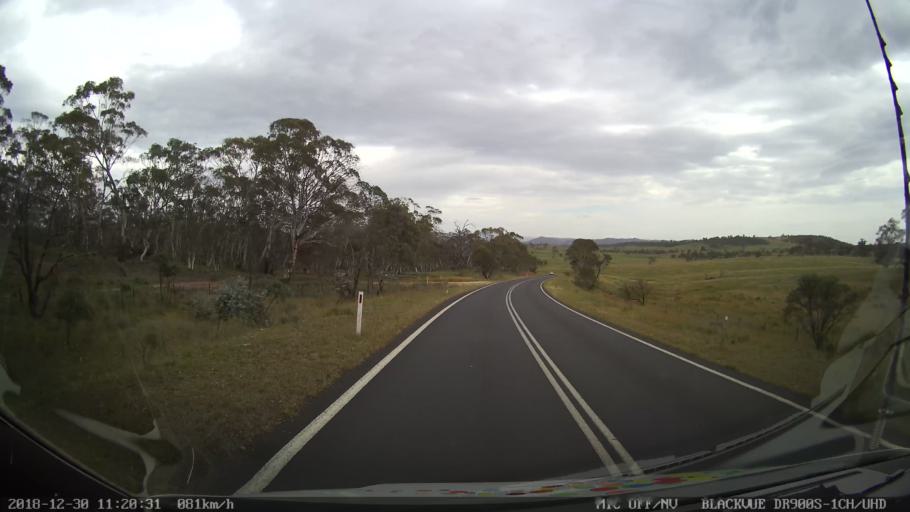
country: AU
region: New South Wales
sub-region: Snowy River
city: Jindabyne
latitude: -36.5174
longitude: 148.6884
